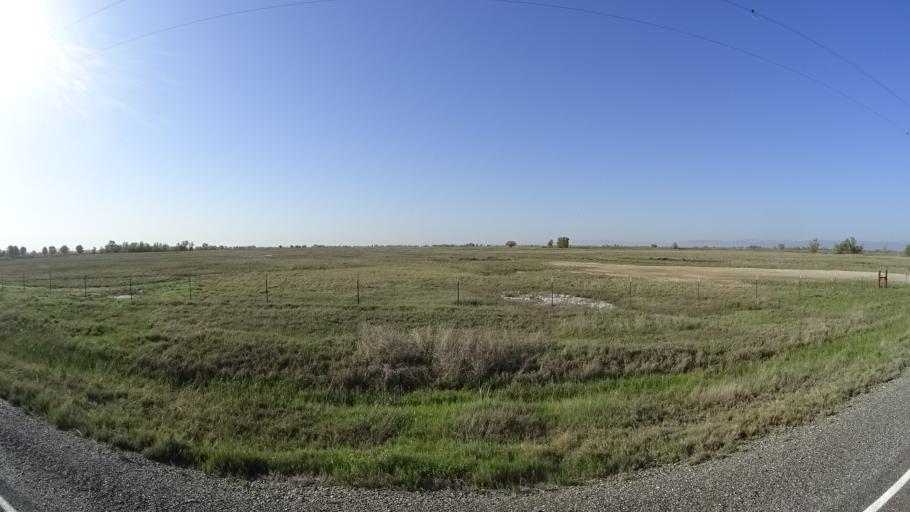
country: US
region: California
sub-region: Glenn County
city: Willows
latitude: 39.4073
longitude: -122.1406
